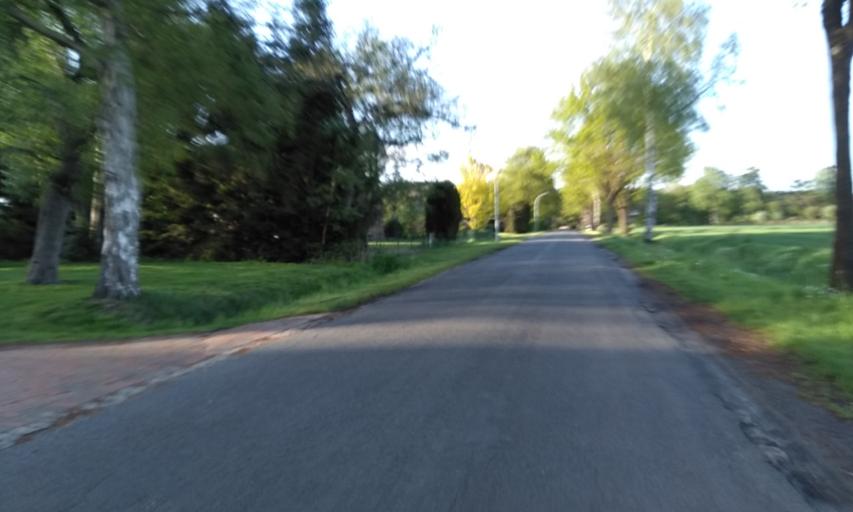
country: DE
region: Lower Saxony
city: Wohnste
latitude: 53.3921
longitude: 9.5047
